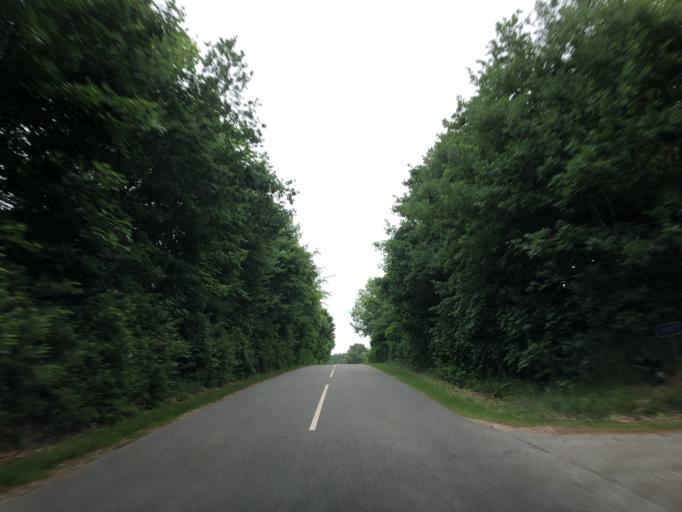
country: DK
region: Central Jutland
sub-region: Holstebro Kommune
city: Holstebro
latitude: 56.2537
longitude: 8.6287
